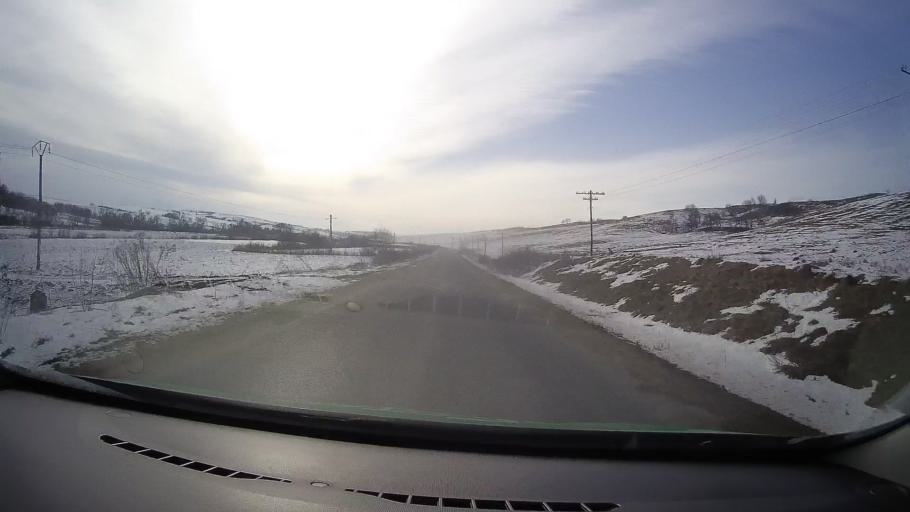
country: RO
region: Sibiu
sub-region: Oras Agnita
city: Ruja
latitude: 45.9955
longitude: 24.6683
